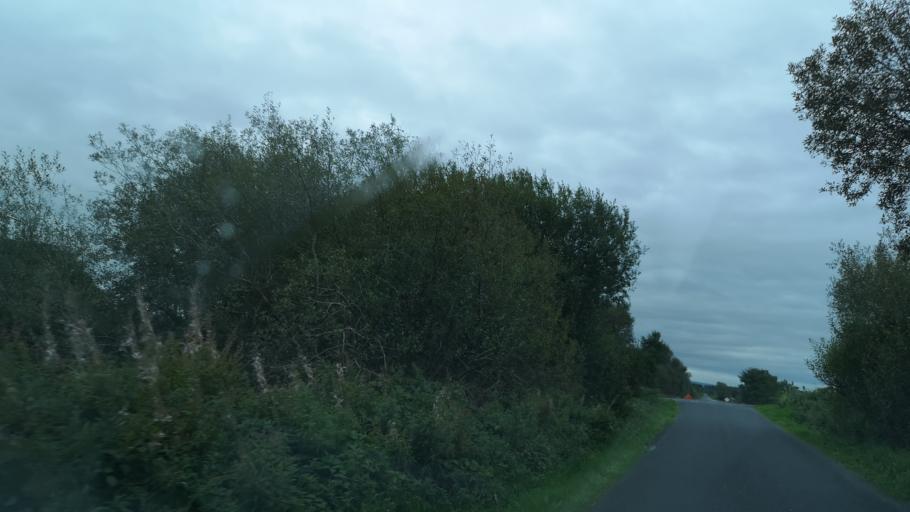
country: IE
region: Leinster
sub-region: Uibh Fhaili
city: Ferbane
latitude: 53.2208
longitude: -7.7270
